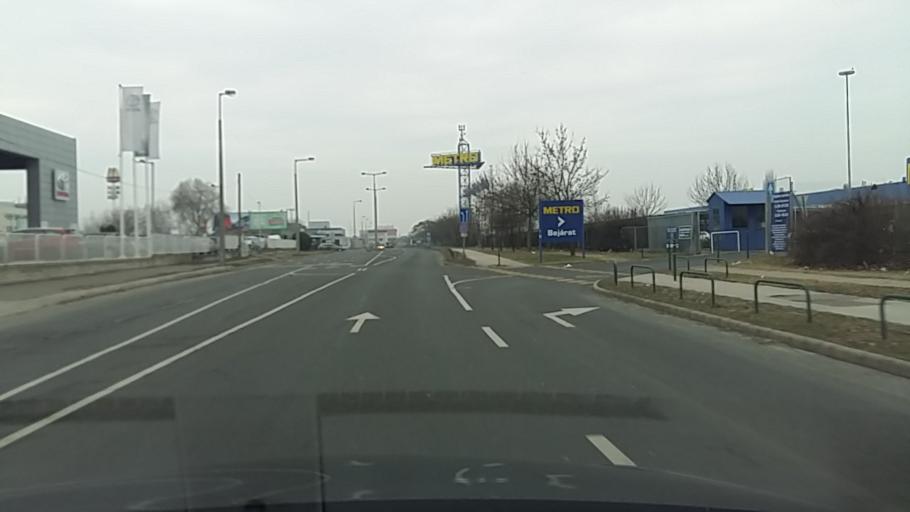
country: HU
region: Budapest
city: Budapest XX. keruelet
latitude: 47.4614
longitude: 19.1075
